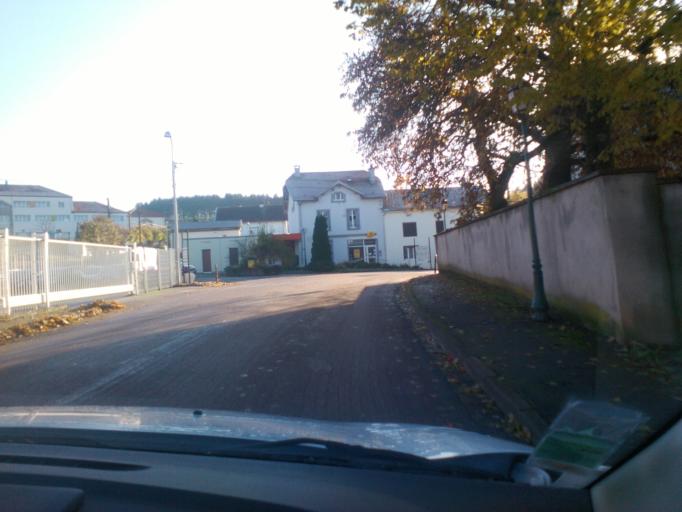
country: FR
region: Lorraine
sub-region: Departement des Vosges
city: Xertigny
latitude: 48.0471
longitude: 6.4010
